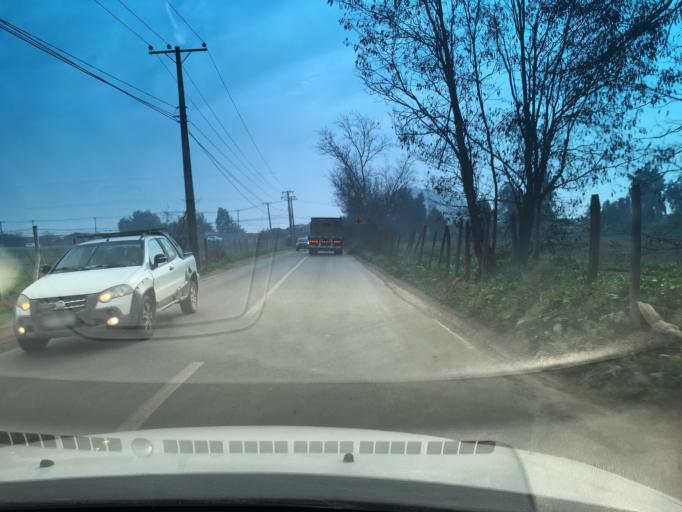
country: CL
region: Santiago Metropolitan
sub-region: Provincia de Chacabuco
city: Lampa
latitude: -33.3530
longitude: -70.8020
